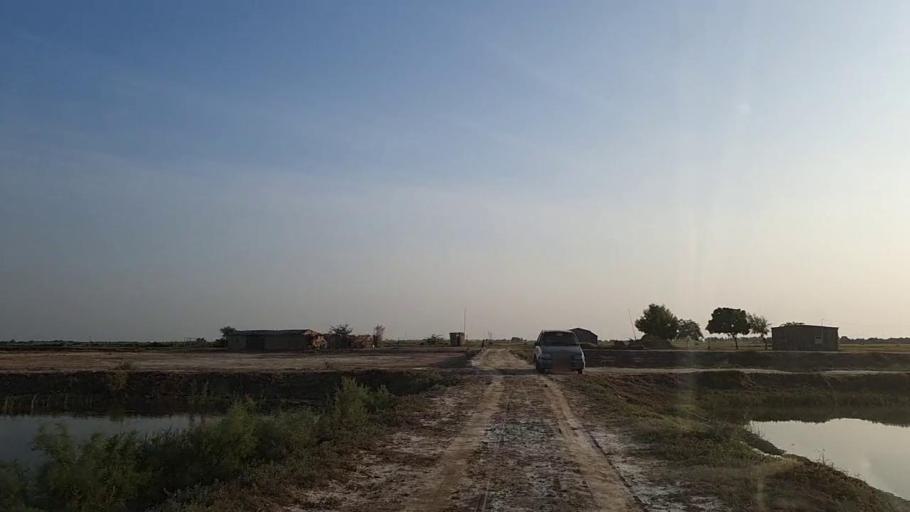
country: PK
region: Sindh
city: Mirpur Batoro
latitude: 24.6059
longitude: 68.1025
